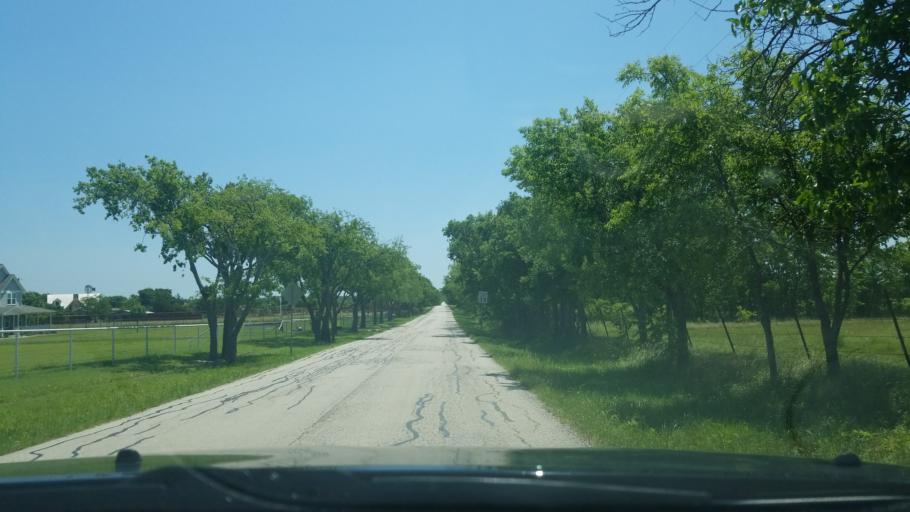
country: US
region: Texas
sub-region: Denton County
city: Krum
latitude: 33.2443
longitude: -97.2565
